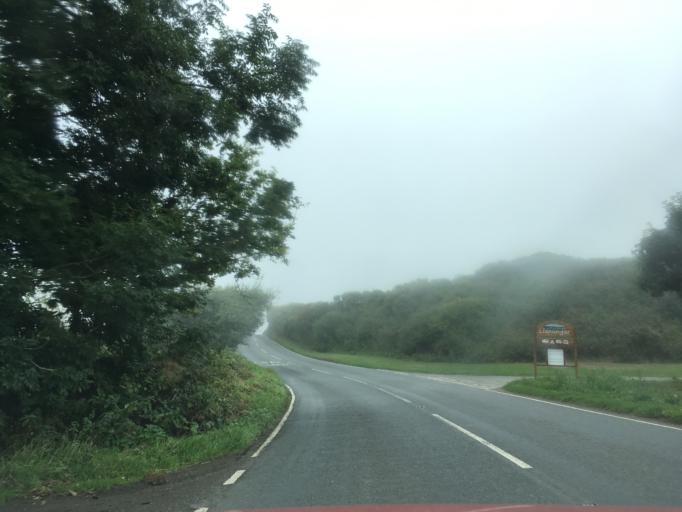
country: GB
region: Wales
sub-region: Pembrokeshire
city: Saint David's
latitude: 51.8772
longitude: -5.2094
